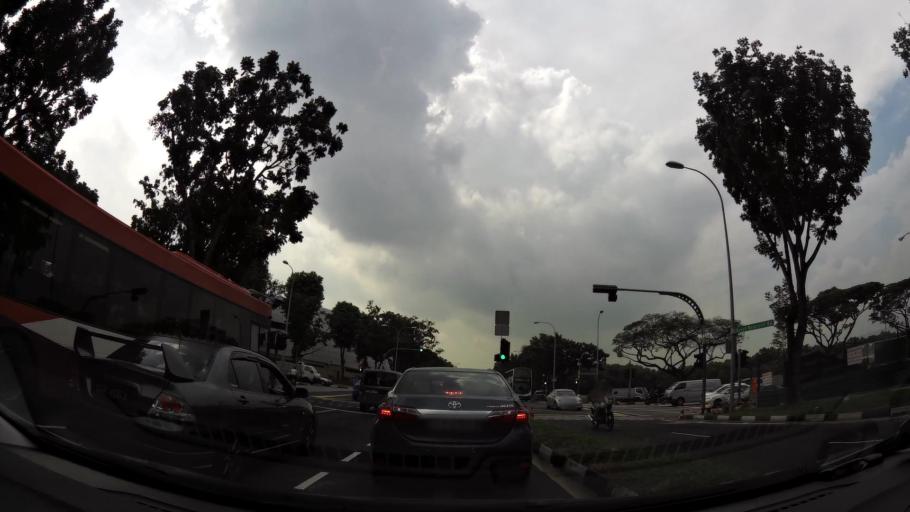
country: SG
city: Singapore
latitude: 1.3383
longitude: 103.9182
